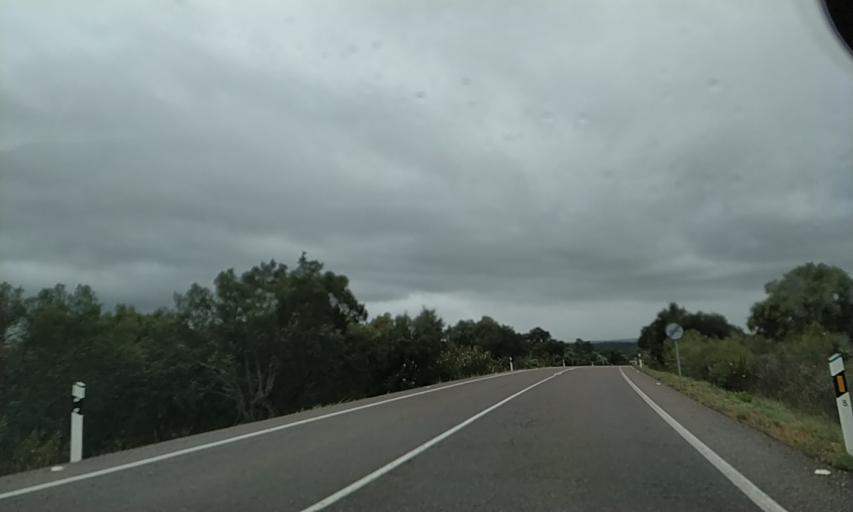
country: ES
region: Extremadura
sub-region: Provincia de Badajoz
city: Puebla de Obando
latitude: 39.1528
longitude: -6.6475
